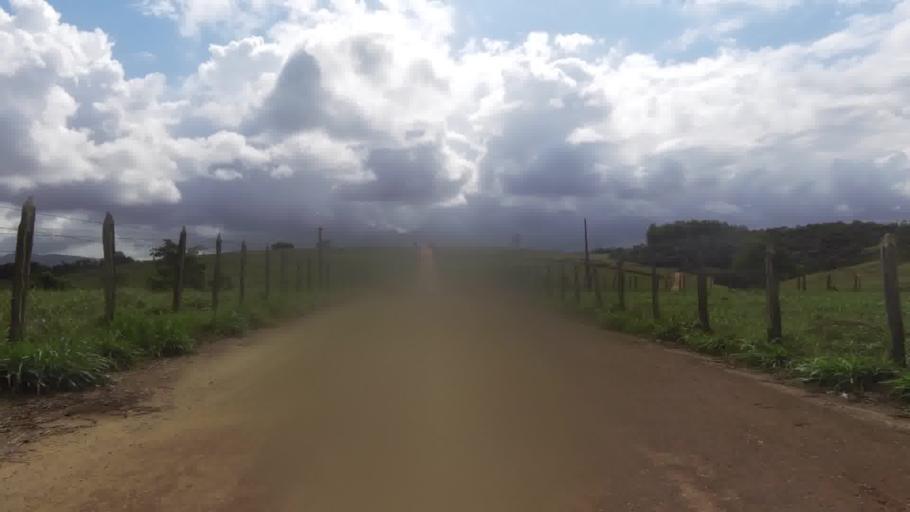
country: BR
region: Espirito Santo
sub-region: Piuma
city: Piuma
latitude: -20.8232
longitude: -40.6983
